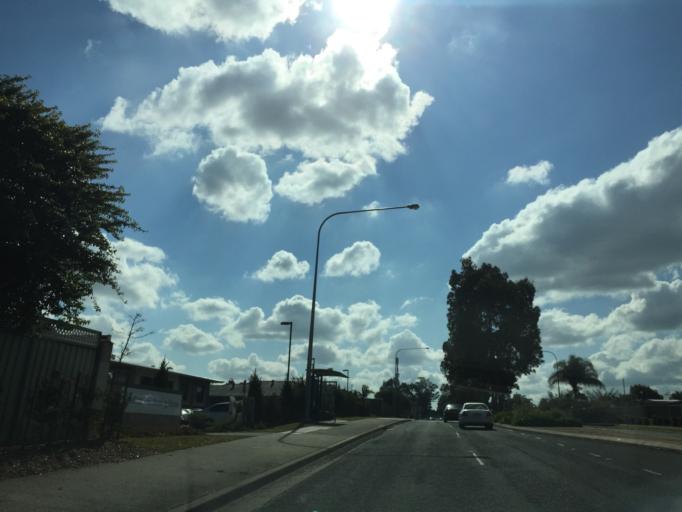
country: AU
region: New South Wales
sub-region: Blacktown
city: Quakers Hill
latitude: -33.7200
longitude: 150.8922
